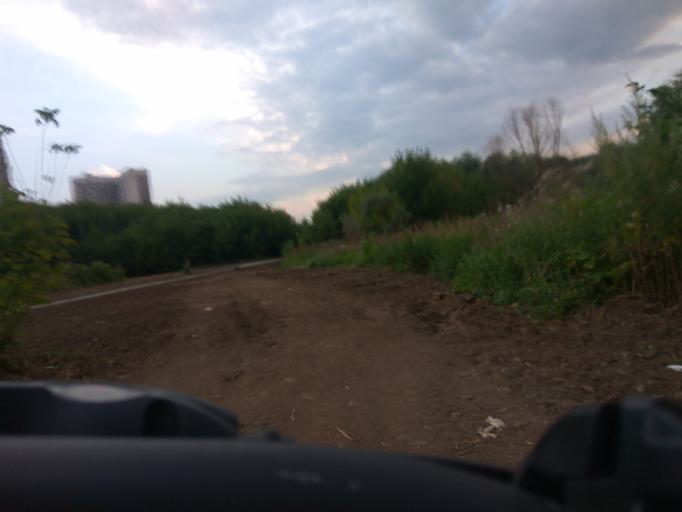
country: RU
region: Moscow
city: Brateyevo
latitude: 55.6403
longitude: 37.7764
